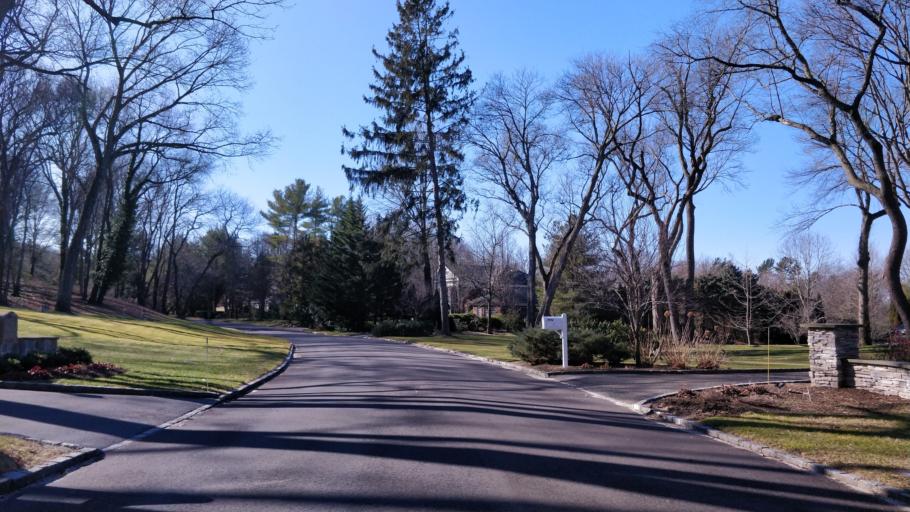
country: US
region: New York
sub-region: Nassau County
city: Brookville
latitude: 40.8129
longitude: -73.5813
